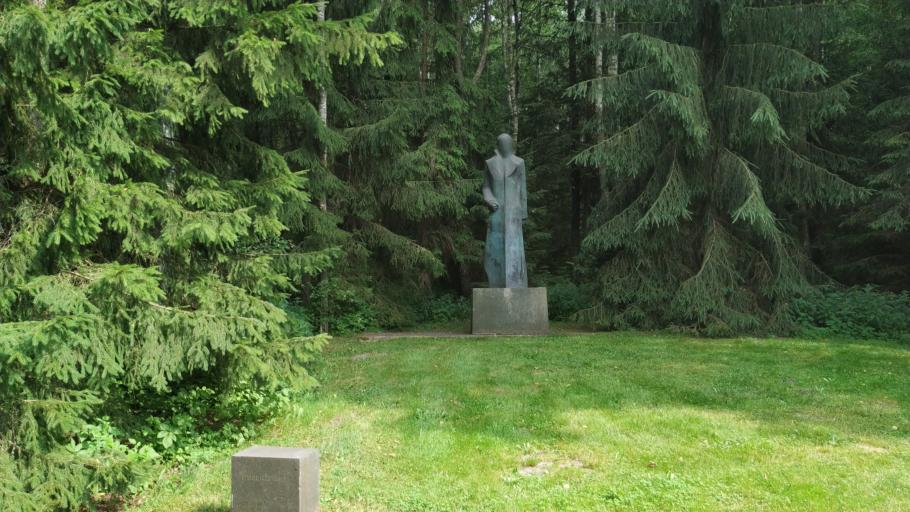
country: LT
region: Alytaus apskritis
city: Druskininkai
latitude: 54.0199
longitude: 24.0769
